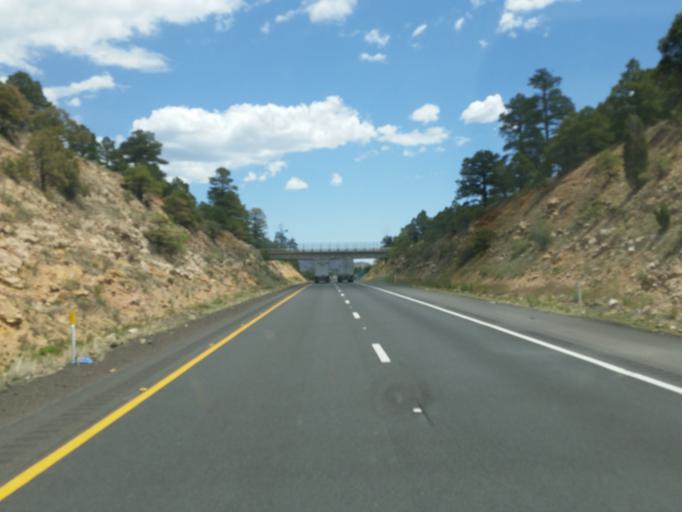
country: US
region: Arizona
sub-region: Coconino County
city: Flagstaff
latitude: 35.2004
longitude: -111.6098
